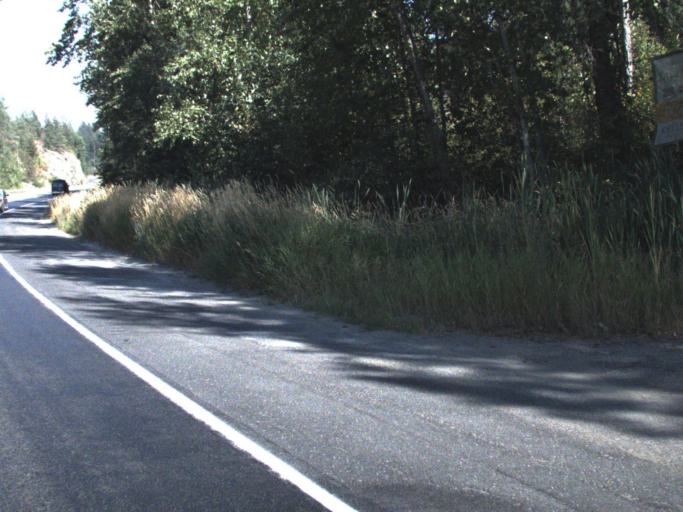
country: US
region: Washington
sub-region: Spokane County
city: Deer Park
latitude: 48.0935
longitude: -117.3226
